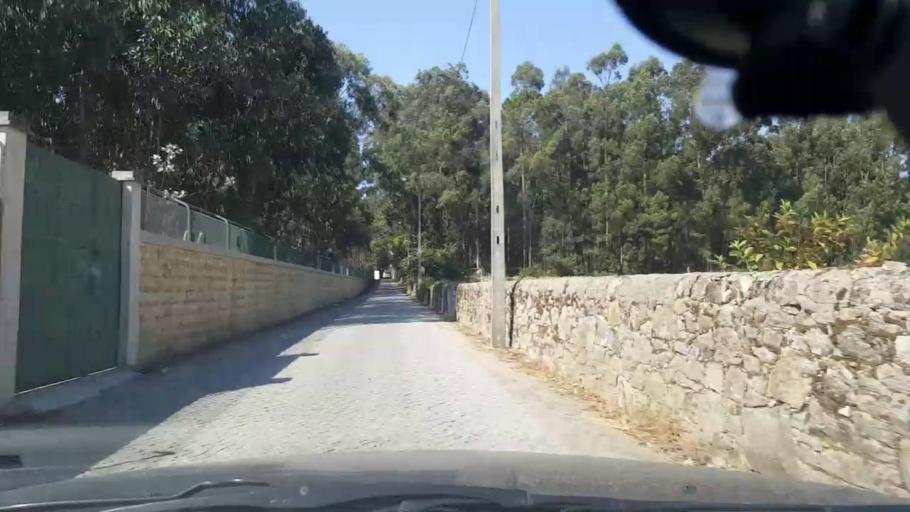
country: PT
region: Porto
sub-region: Povoa de Varzim
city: Pedroso
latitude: 41.3917
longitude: -8.7127
